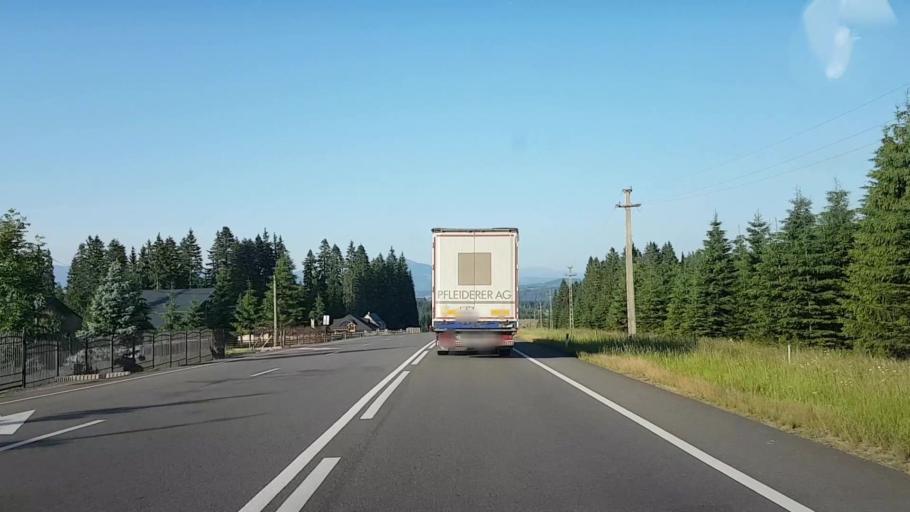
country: RO
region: Suceava
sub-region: Comuna Poiana Stampei
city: Poiana Stampei
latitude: 47.2958
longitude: 25.0854
